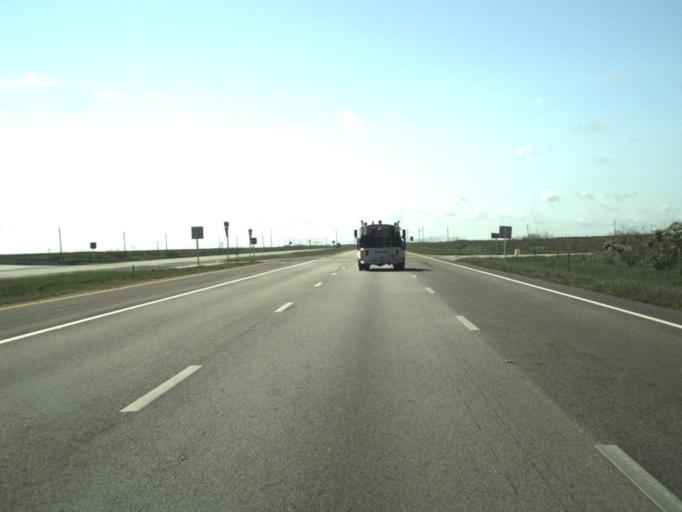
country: US
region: Florida
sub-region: Palm Beach County
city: Belle Glade Camp
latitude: 26.3705
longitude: -80.5655
